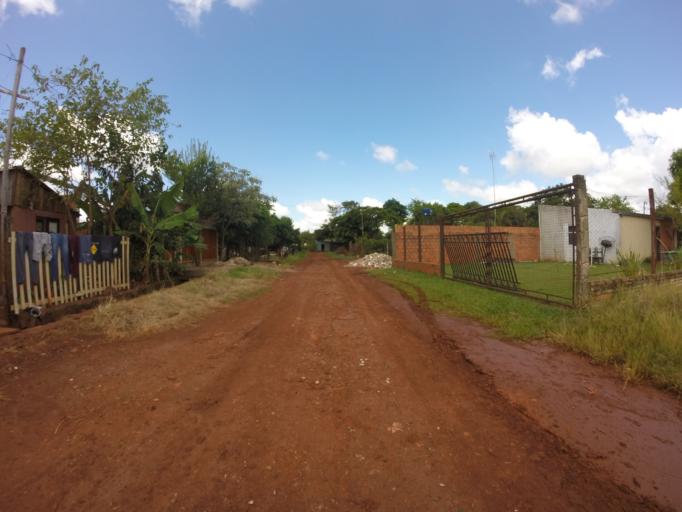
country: PY
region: Alto Parana
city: Ciudad del Este
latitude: -25.4007
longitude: -54.6339
